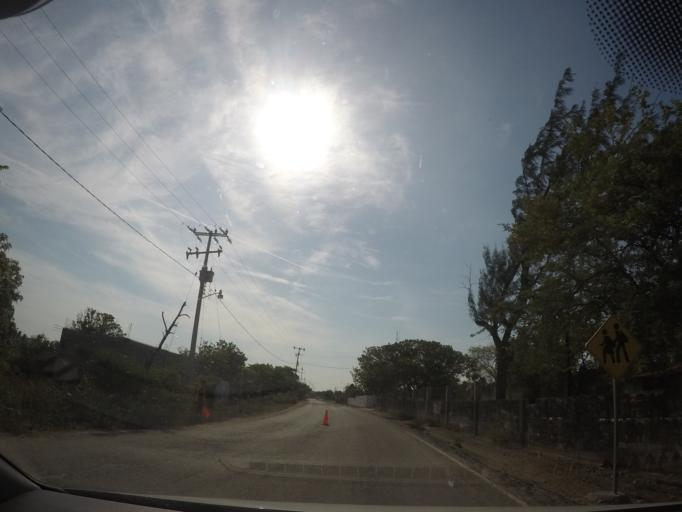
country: MX
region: Oaxaca
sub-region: Salina Cruz
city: Salina Cruz
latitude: 16.2205
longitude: -95.1304
